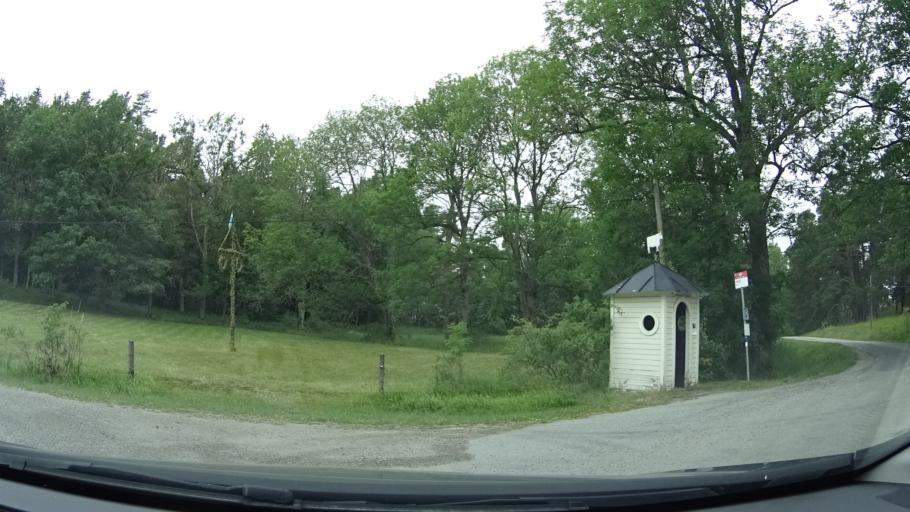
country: SE
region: Stockholm
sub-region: Varmdo Kommun
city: Mortnas
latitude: 59.3794
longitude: 18.4592
